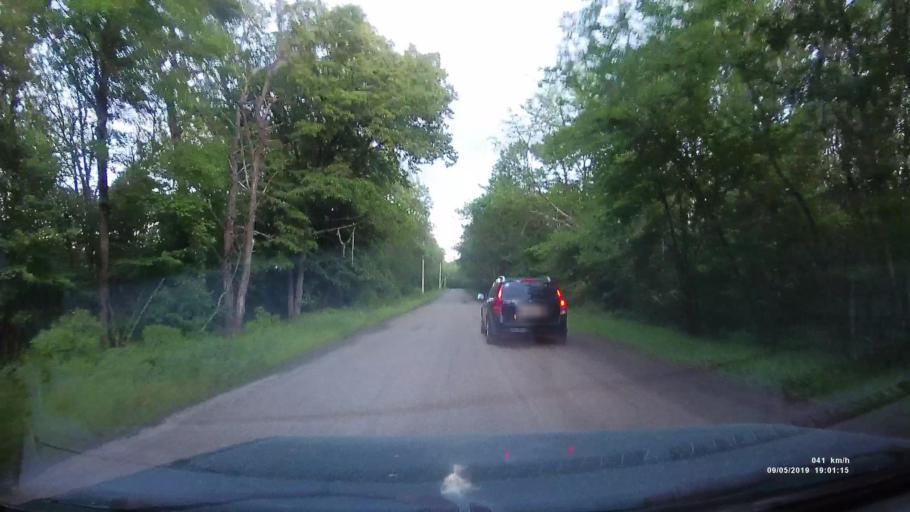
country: RU
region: Krasnodarskiy
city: Kanelovskaya
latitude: 46.7488
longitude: 39.1426
